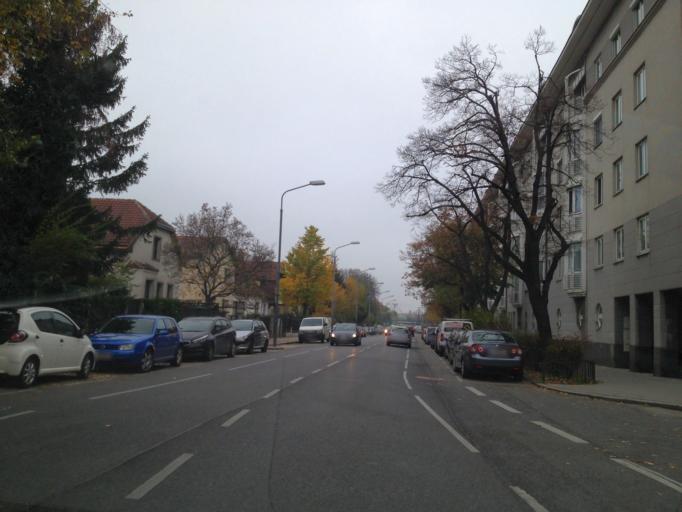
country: AT
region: Vienna
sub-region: Wien Stadt
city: Vienna
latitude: 48.2547
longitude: 16.3935
